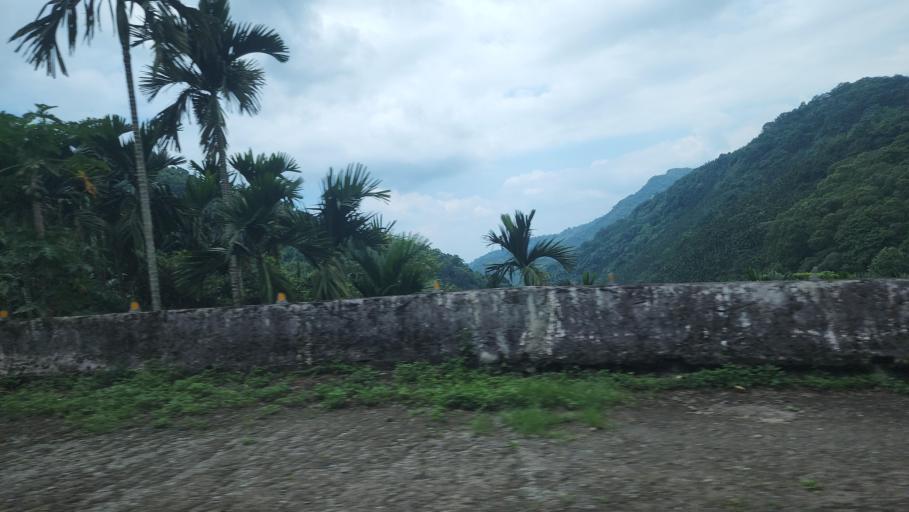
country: TW
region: Taipei
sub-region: Taipei
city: Banqiao
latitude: 24.8963
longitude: 121.4251
